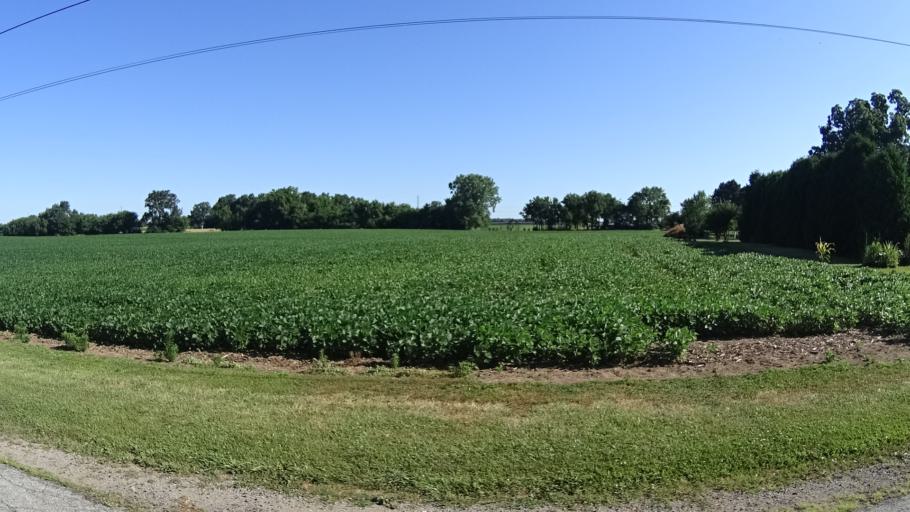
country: US
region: Ohio
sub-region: Erie County
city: Sandusky
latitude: 41.3776
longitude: -82.7430
